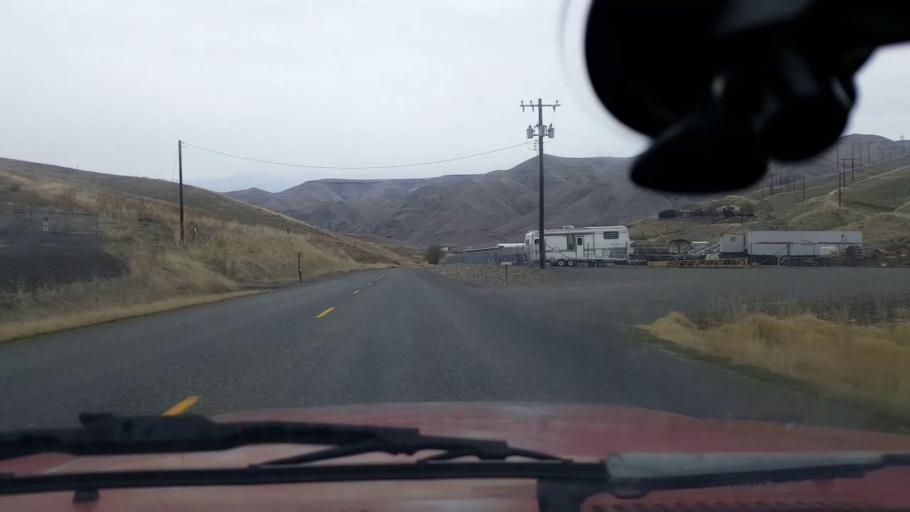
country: US
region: Washington
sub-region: Asotin County
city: Clarkston Heights-Vineland
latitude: 46.4118
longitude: -117.1118
